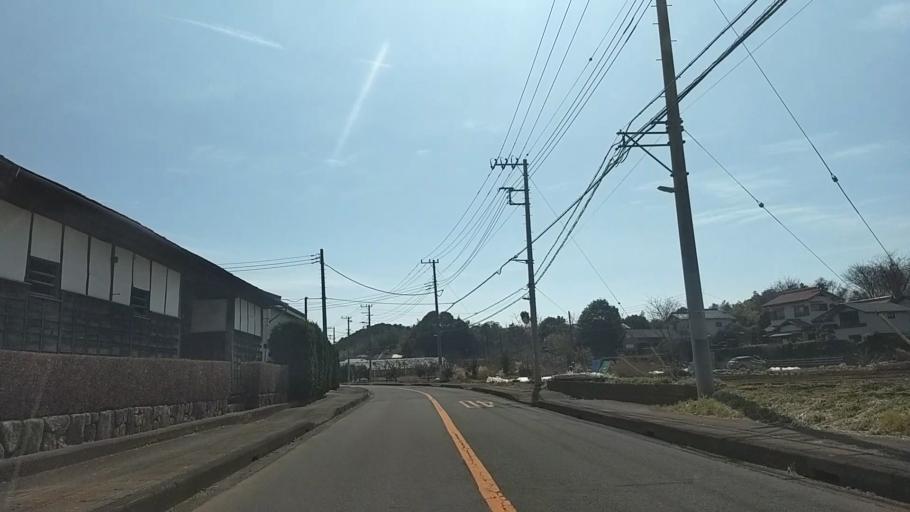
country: JP
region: Kanagawa
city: Fujisawa
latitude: 35.3808
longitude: 139.4291
